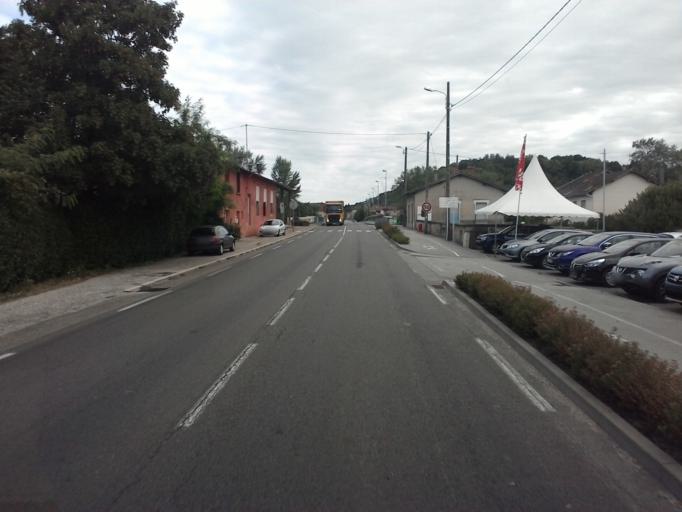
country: FR
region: Rhone-Alpes
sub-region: Departement de l'Ain
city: Ambronay
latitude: 46.0452
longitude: 5.3363
